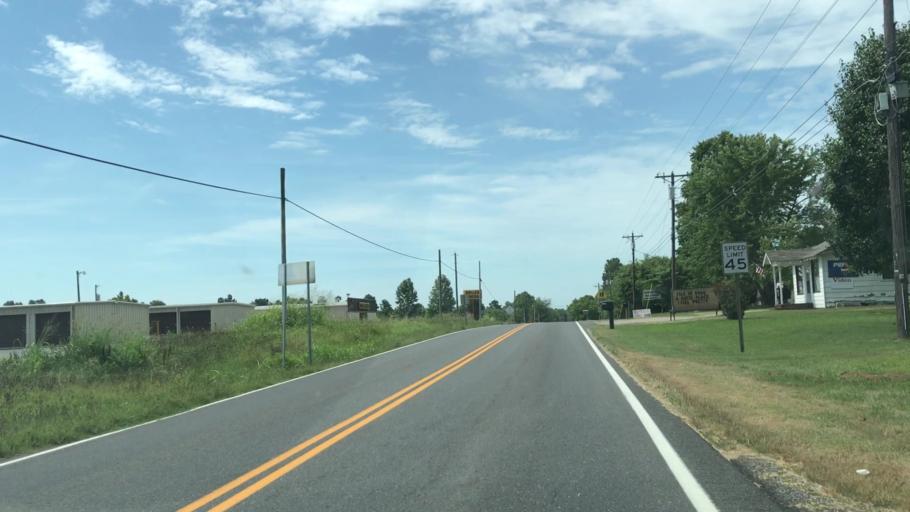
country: US
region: Kentucky
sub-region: McCracken County
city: Reidland
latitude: 36.9195
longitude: -88.5202
